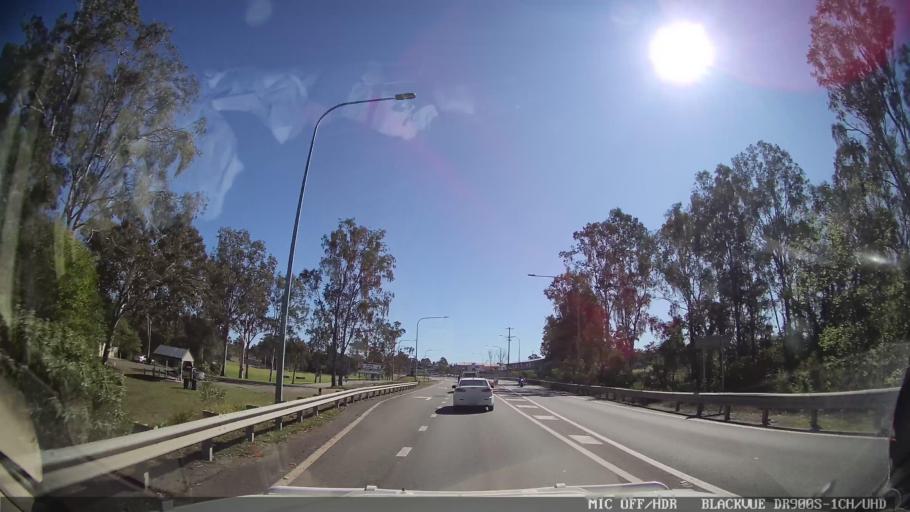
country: AU
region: Queensland
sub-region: Gympie Regional Council
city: Monkland
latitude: -26.2323
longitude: 152.6978
